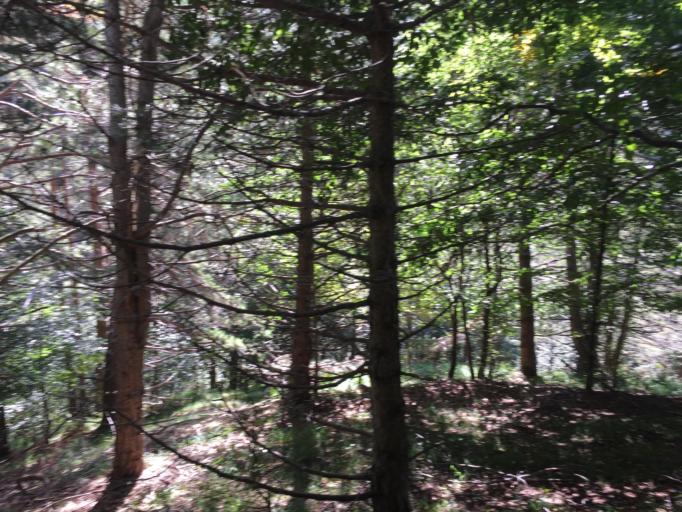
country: IT
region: Friuli Venezia Giulia
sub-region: Provincia di Udine
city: Chiusaforte
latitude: 46.4220
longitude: 13.2767
